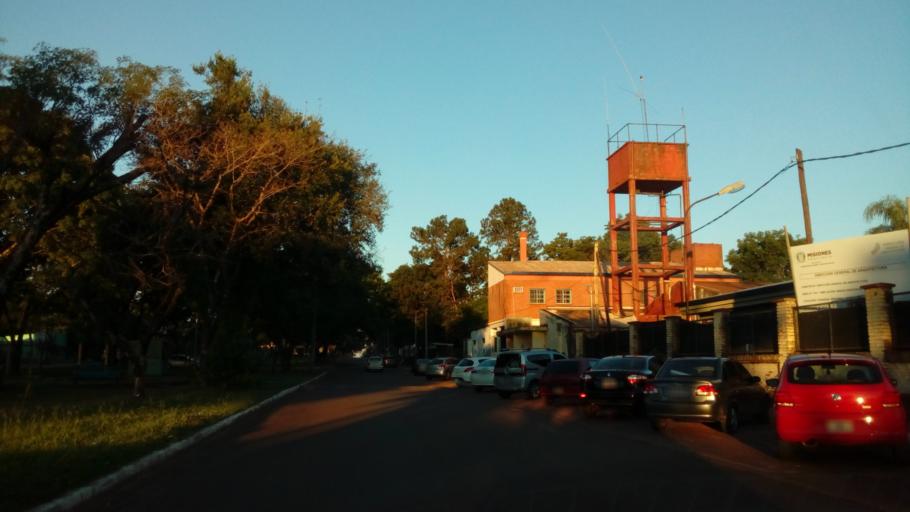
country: AR
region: Misiones
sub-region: Departamento de Capital
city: Posadas
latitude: -27.4328
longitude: -55.8854
